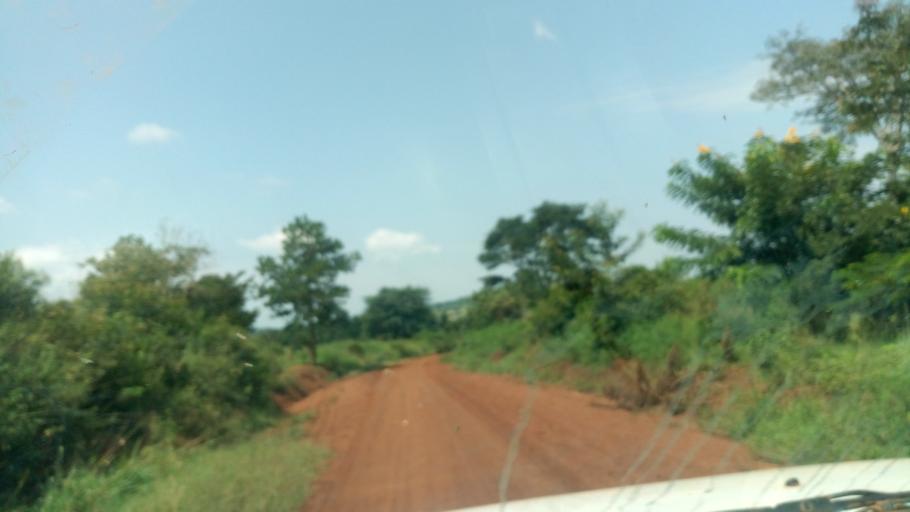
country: UG
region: Western Region
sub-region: Masindi District
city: Masindi
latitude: 1.6751
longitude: 31.8289
